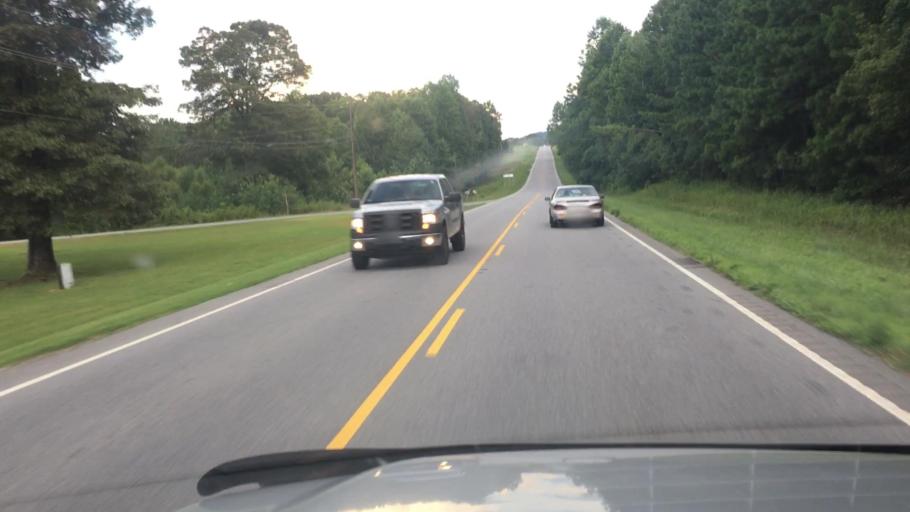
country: US
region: South Carolina
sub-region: Spartanburg County
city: Mayo
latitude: 35.1369
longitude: -81.8062
